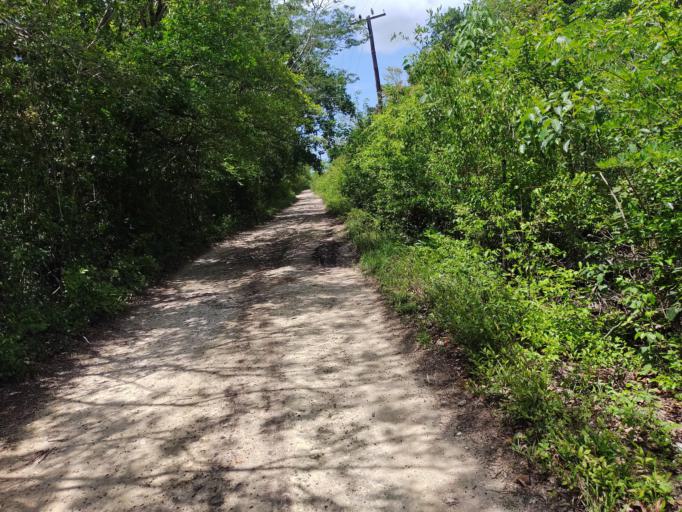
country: MX
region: Quintana Roo
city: San Miguel de Cozumel
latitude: 20.4998
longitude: -86.9011
